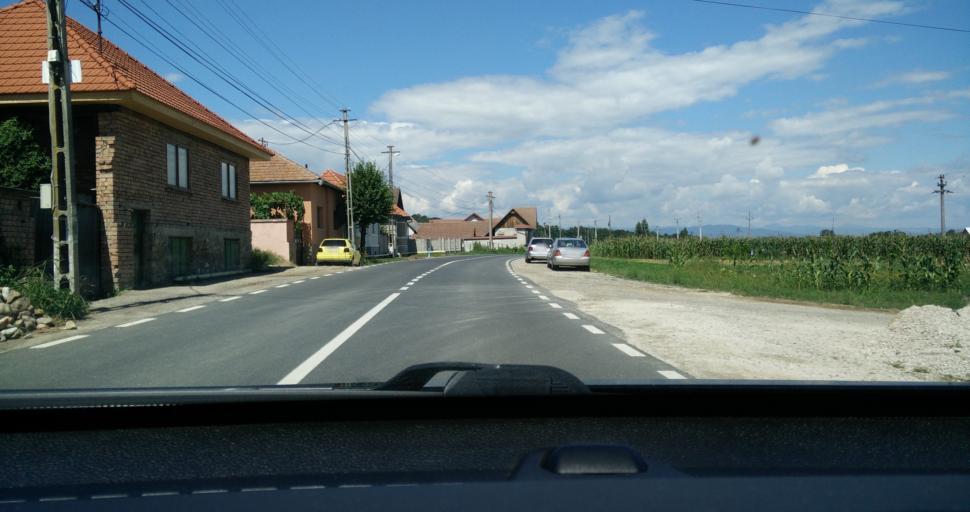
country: RO
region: Alba
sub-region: Comuna Sasciori
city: Sebesel
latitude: 45.8913
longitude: 23.5620
